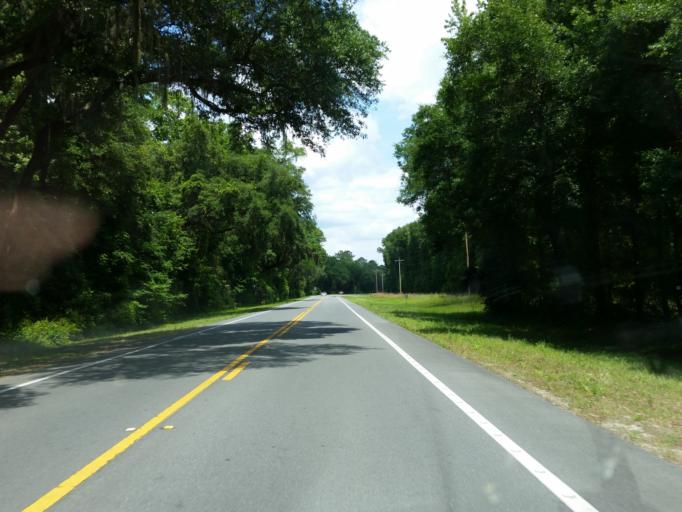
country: US
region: Florida
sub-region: Alachua County
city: Gainesville
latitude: 29.5657
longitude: -82.3929
